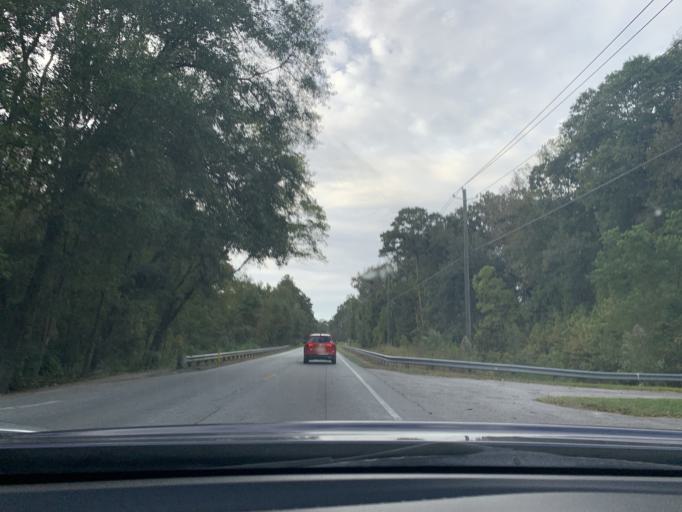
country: US
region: Georgia
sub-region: Chatham County
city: Georgetown
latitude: 32.0309
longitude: -81.2505
